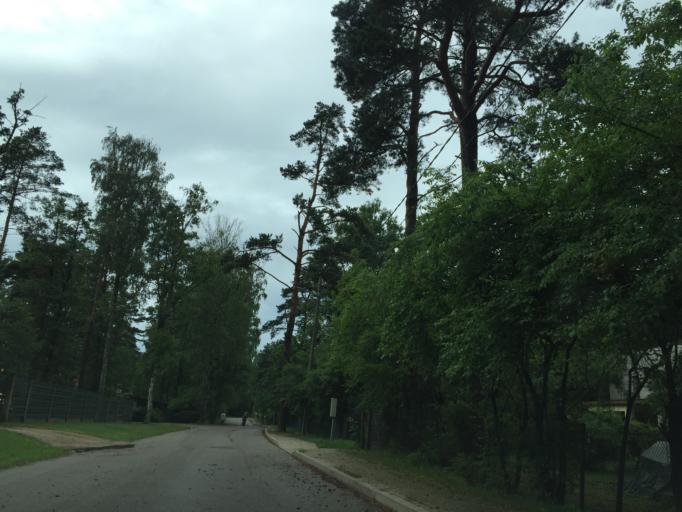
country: LV
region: Riga
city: Jaunciems
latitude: 57.0792
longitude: 24.1188
